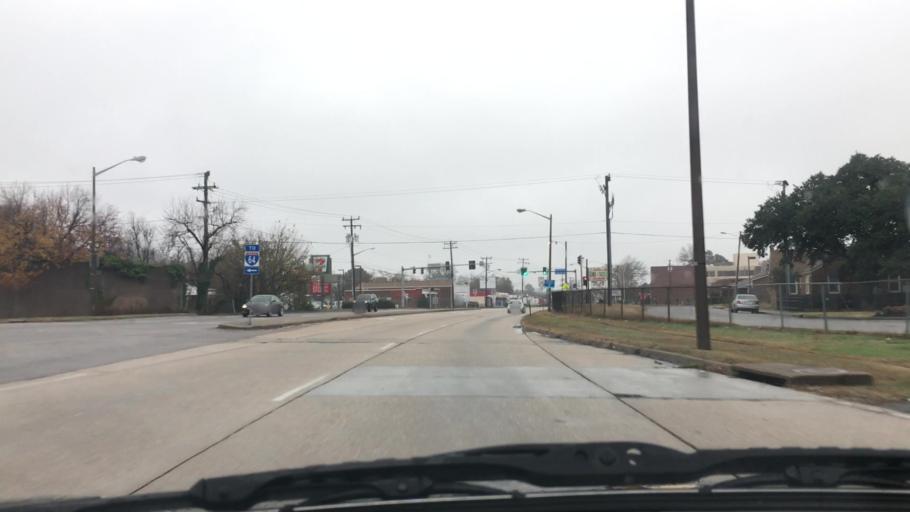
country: US
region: Virginia
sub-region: City of Norfolk
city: Norfolk
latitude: 36.9084
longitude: -76.2564
